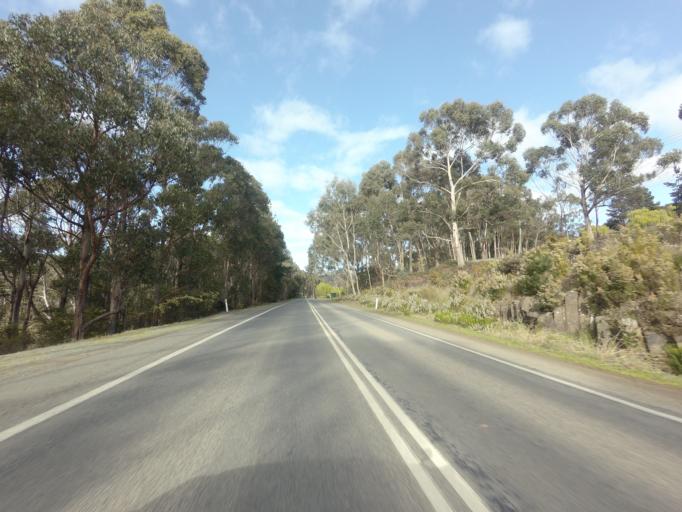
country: AU
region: Tasmania
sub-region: Huon Valley
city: Geeveston
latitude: -43.1615
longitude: 146.9512
